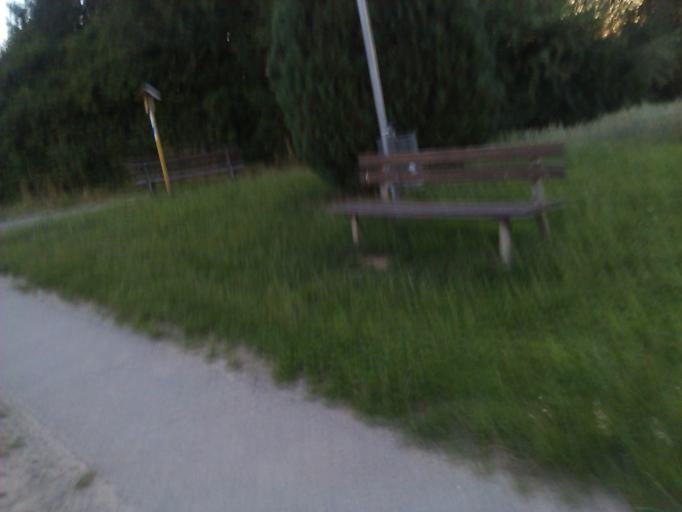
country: DE
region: Baden-Wuerttemberg
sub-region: Regierungsbezirk Stuttgart
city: Oedheim
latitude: 49.2493
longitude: 9.2259
